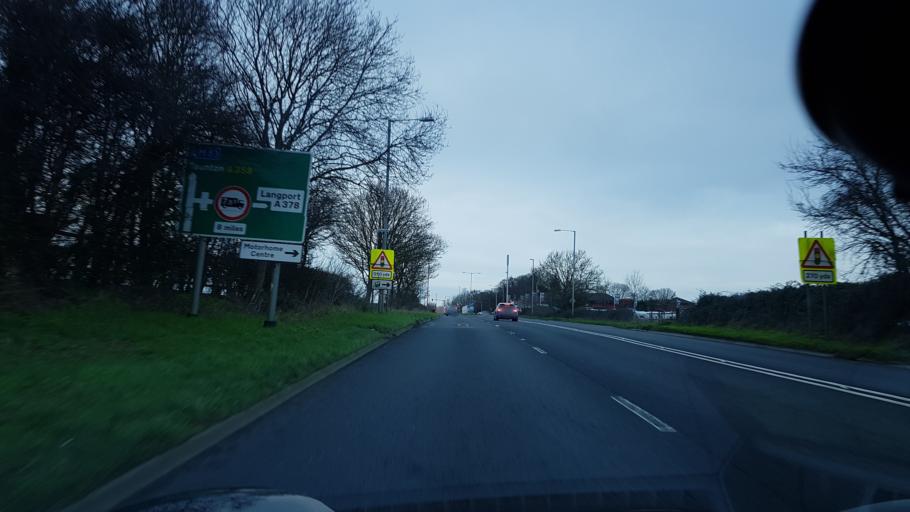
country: GB
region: England
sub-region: Somerset
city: Creech Saint Michael
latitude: 50.9977
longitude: -3.0186
